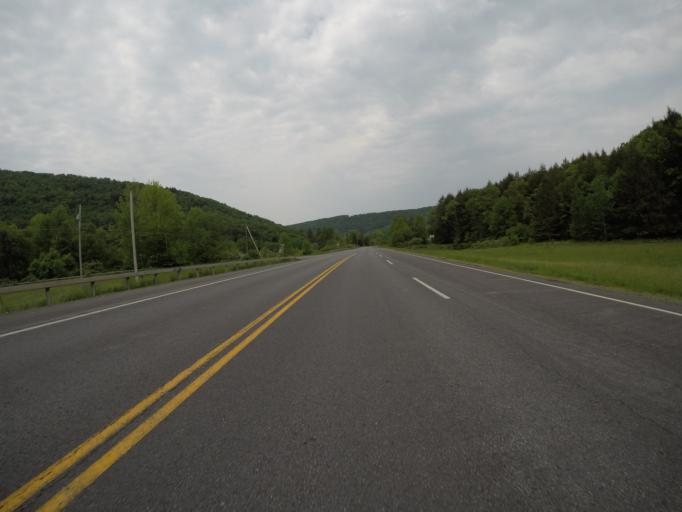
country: US
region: New York
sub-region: Sullivan County
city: Livingston Manor
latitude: 41.9684
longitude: -74.8992
